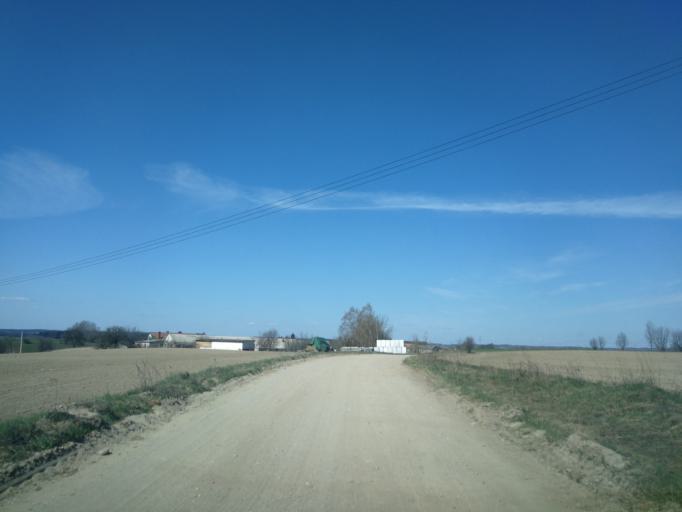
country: PL
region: Warmian-Masurian Voivodeship
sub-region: Powiat dzialdowski
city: Rybno
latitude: 53.4356
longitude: 19.9630
